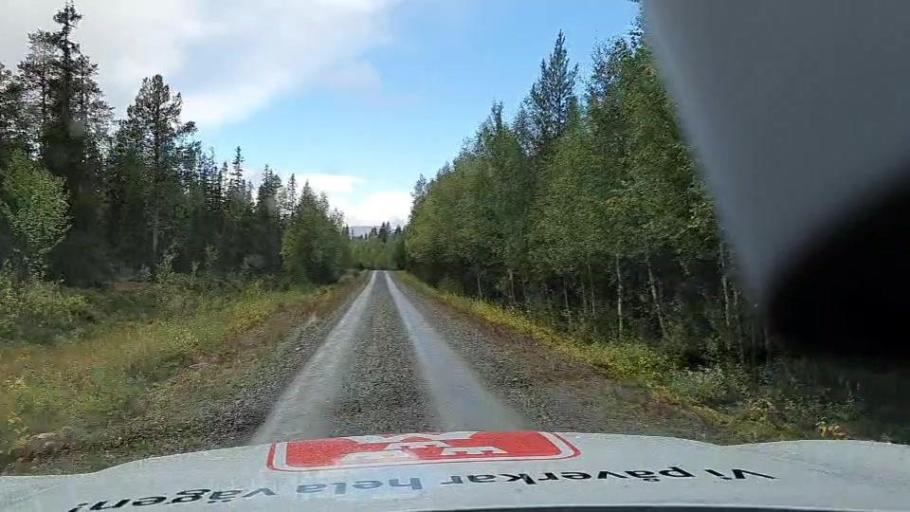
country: SE
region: Jaemtland
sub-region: Are Kommun
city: Are
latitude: 63.1886
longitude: 13.2437
